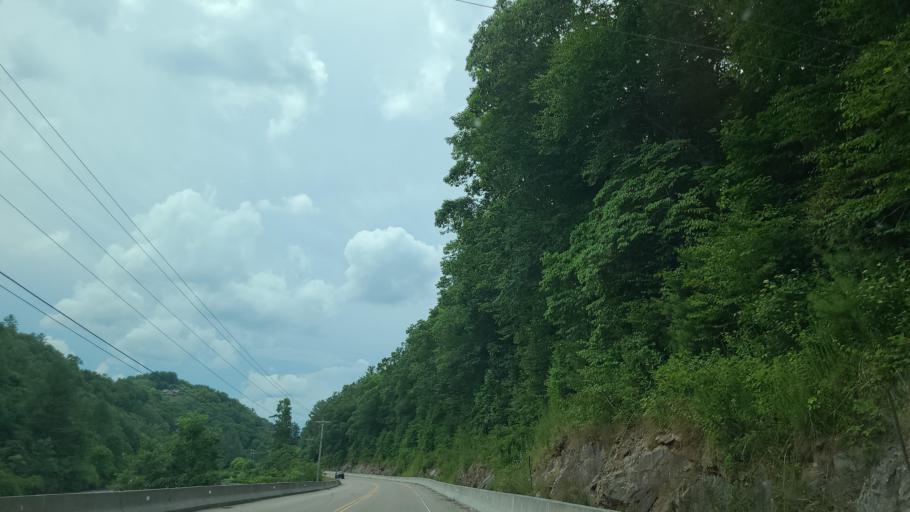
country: US
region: North Carolina
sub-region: Ashe County
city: Jefferson
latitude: 36.3761
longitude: -81.3979
